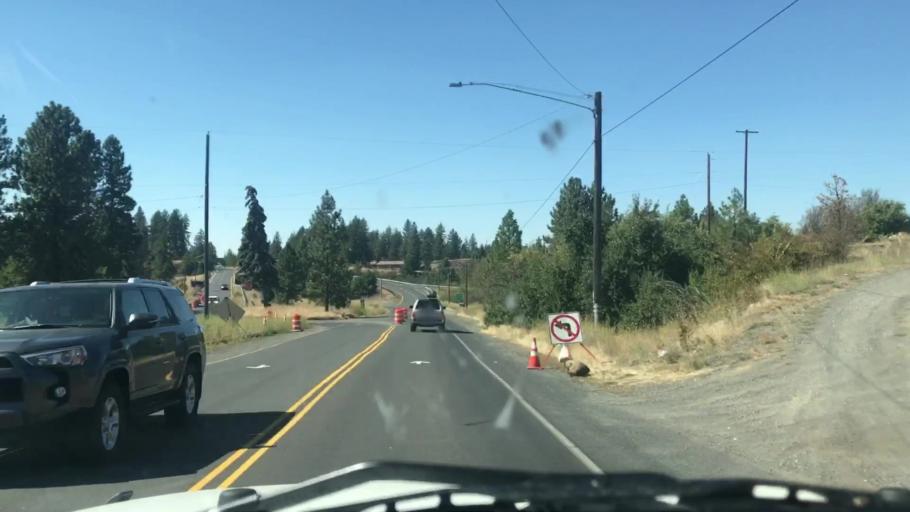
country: US
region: Washington
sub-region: Spokane County
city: Spokane
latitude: 47.6416
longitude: -117.4801
